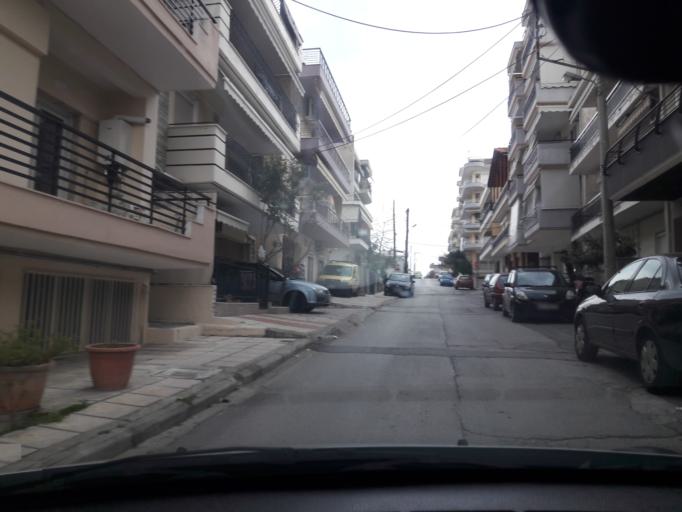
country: GR
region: Central Macedonia
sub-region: Nomos Thessalonikis
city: Stavroupoli
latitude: 40.6687
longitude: 22.9232
